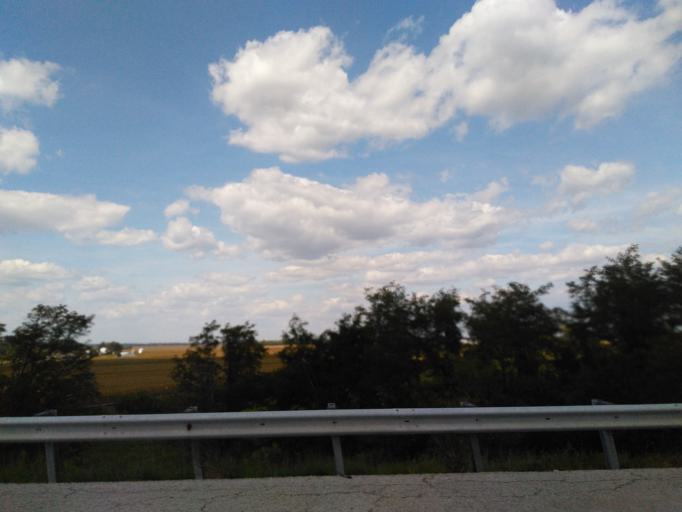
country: US
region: Illinois
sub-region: Monroe County
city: Columbia
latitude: 38.4749
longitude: -90.2308
